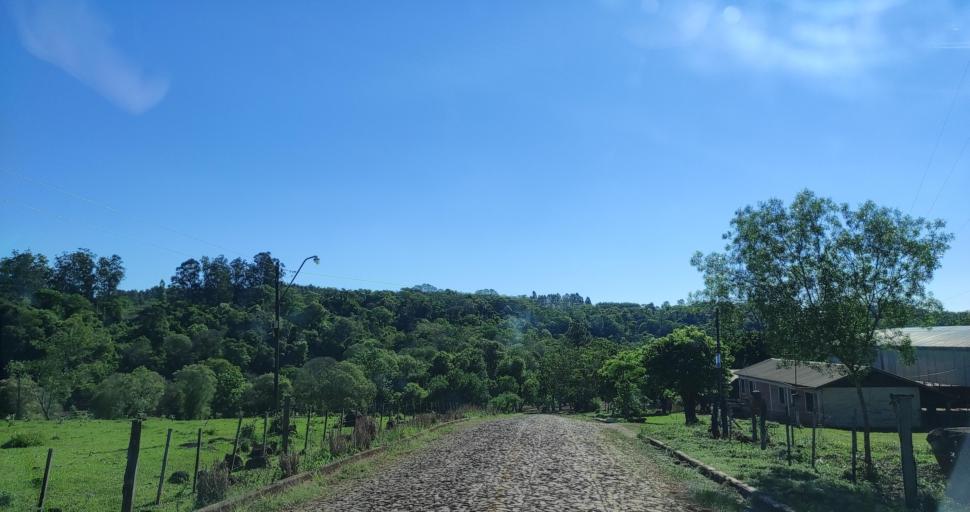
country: AR
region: Misiones
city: Capiovi
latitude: -26.9210
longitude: -55.0775
